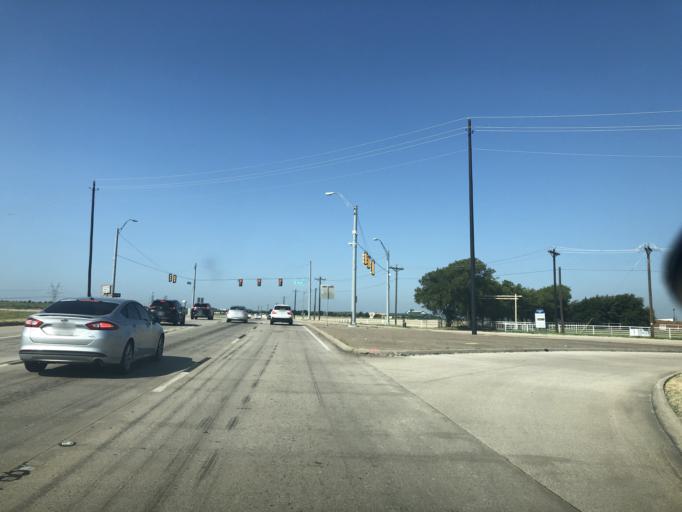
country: US
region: Texas
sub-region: Tarrant County
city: Haslet
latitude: 32.9652
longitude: -97.2976
